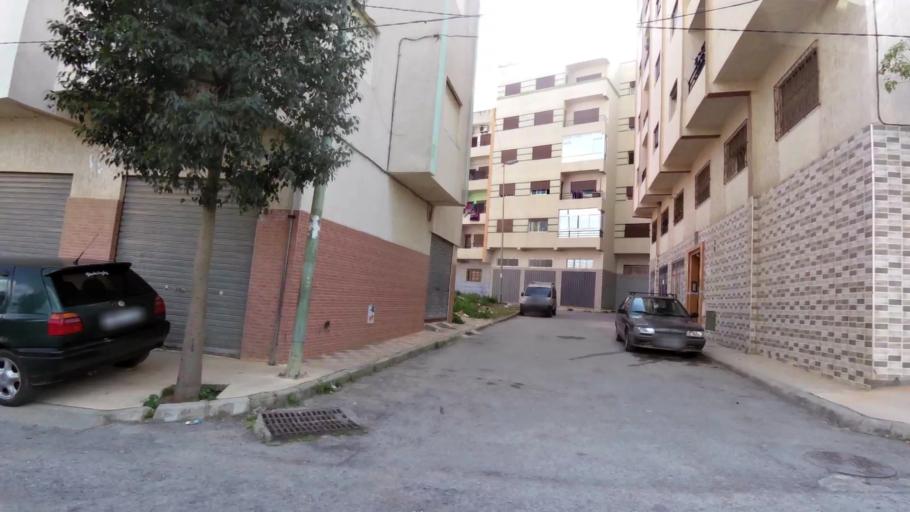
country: MA
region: Tanger-Tetouan
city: Tetouan
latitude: 35.5893
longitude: -5.3477
